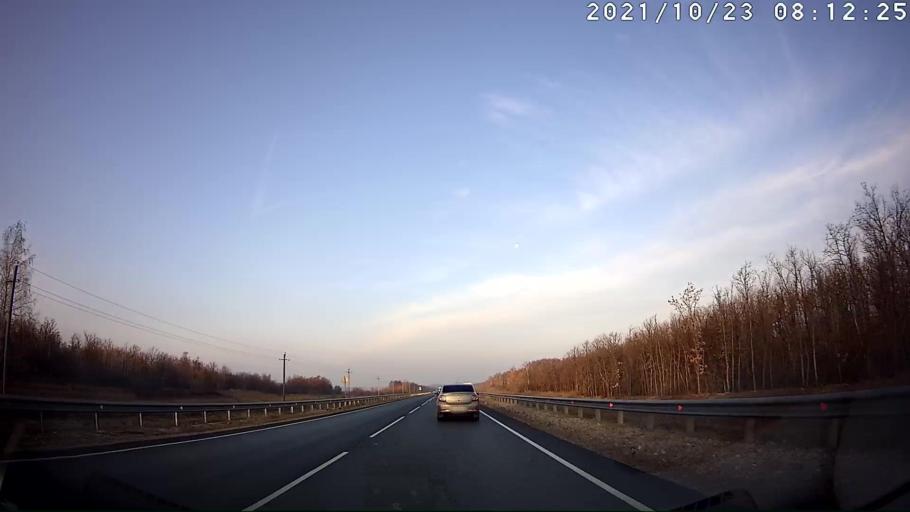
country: RU
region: Saratov
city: Shikhany
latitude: 52.1613
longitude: 47.1596
